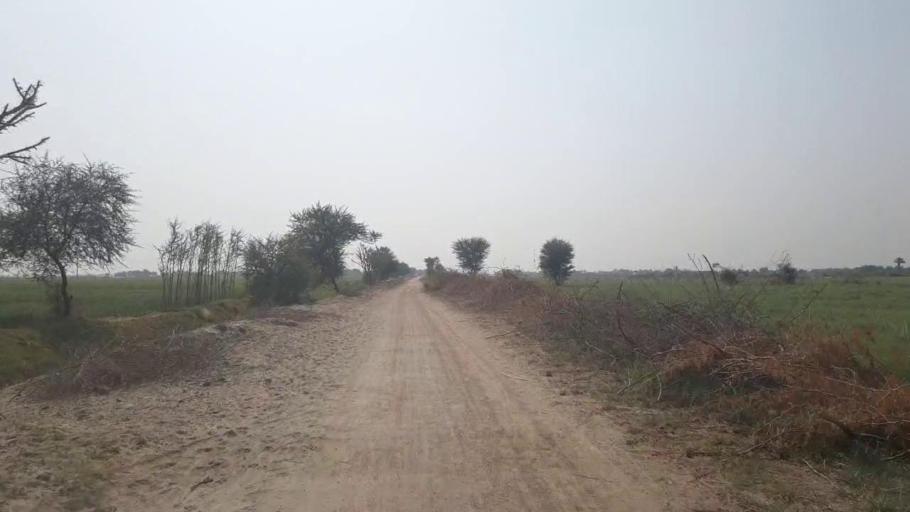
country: PK
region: Sindh
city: Dhoro Naro
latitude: 25.4440
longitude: 69.6256
